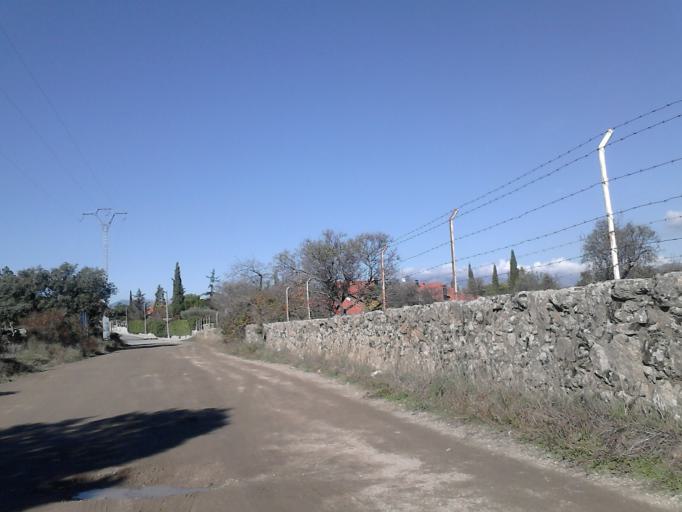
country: ES
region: Madrid
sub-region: Provincia de Madrid
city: Galapagar
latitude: 40.5659
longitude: -3.9959
